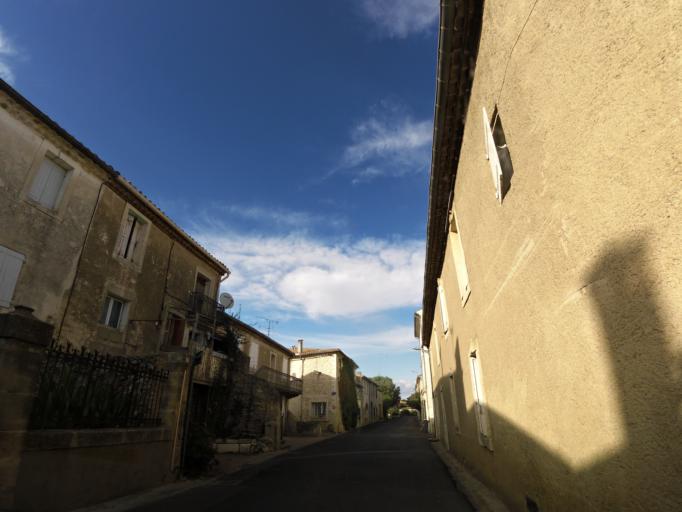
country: FR
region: Languedoc-Roussillon
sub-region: Departement de l'Herault
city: Beaulieu
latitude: 43.7709
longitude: 4.0218
